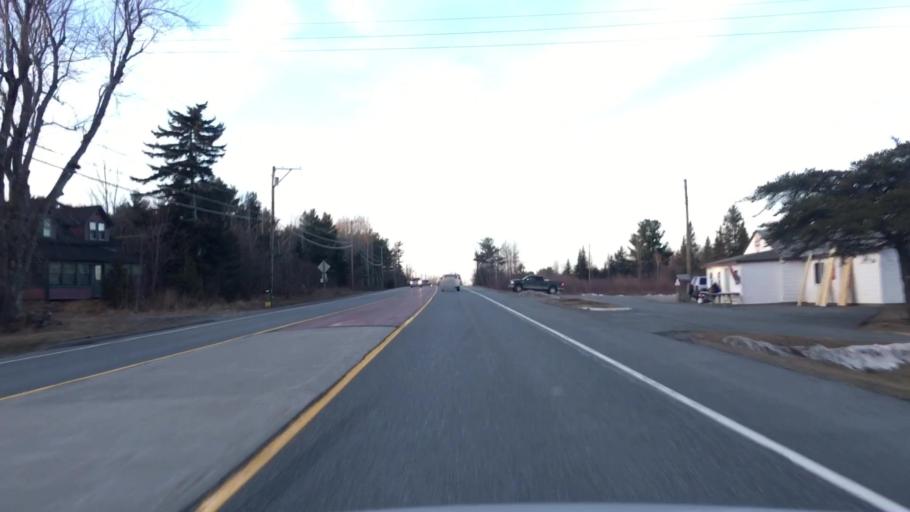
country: US
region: Maine
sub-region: Hancock County
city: Surry
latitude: 44.6171
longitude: -68.5266
